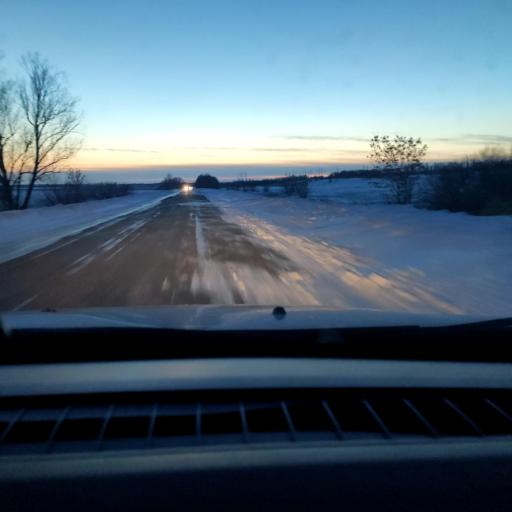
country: RU
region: Samara
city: Georgiyevka
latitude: 53.3370
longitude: 50.9418
